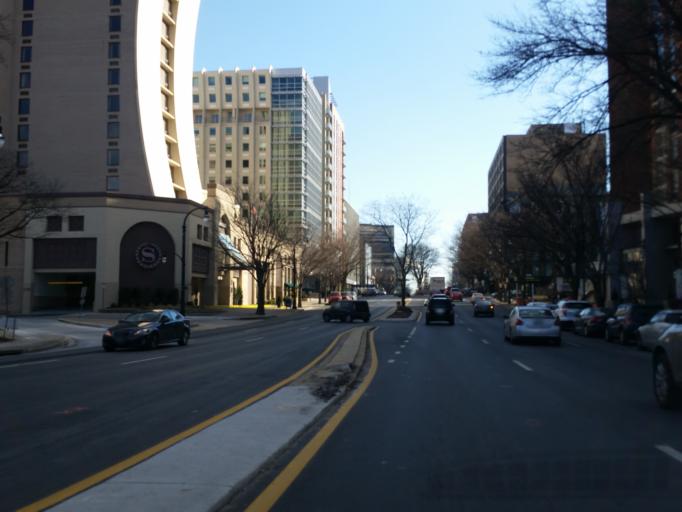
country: US
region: Maryland
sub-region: Montgomery County
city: Silver Spring
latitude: 38.9992
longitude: -77.0316
